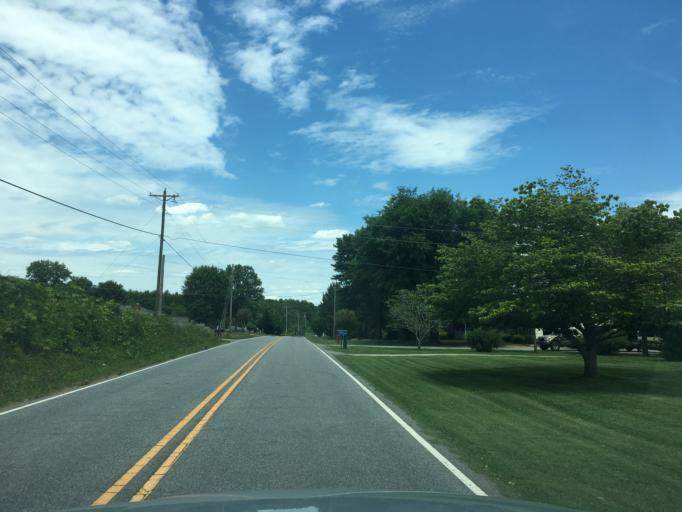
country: US
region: North Carolina
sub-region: Burke County
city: Glen Alpine
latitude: 35.6802
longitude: -81.7693
